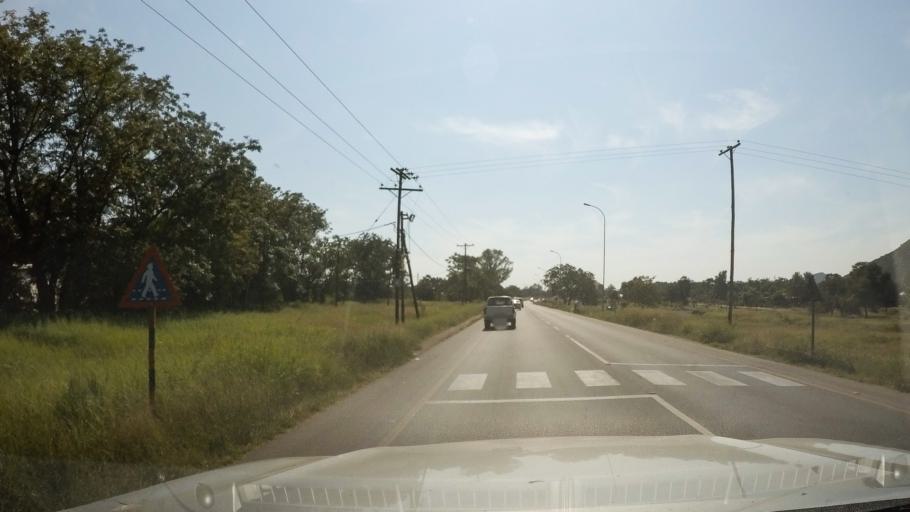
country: BW
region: South East
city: Lobatse
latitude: -25.2180
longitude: 25.6806
